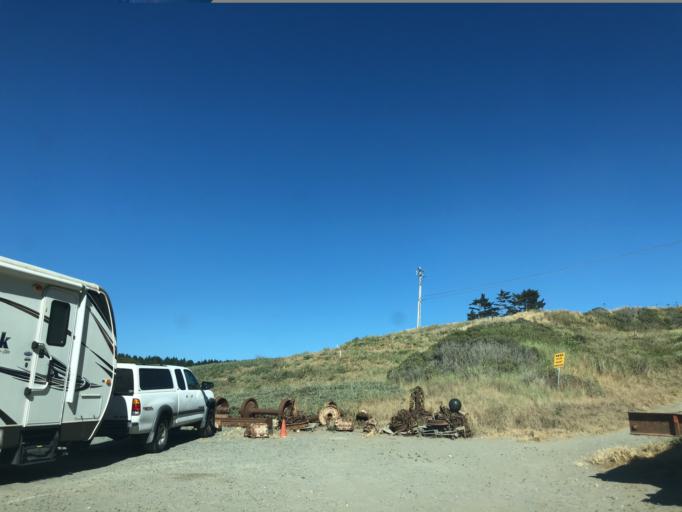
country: US
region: California
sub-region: Humboldt County
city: Westhaven-Moonstone
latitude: 41.0568
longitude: -124.1493
